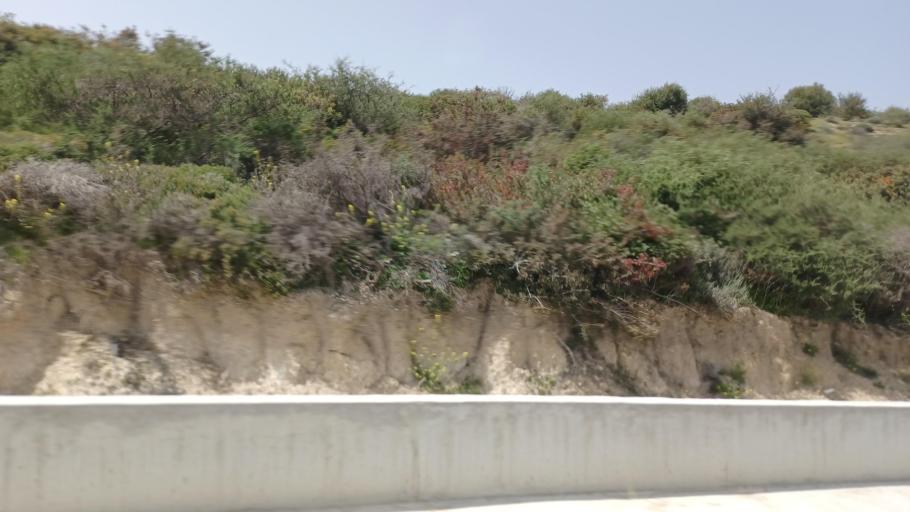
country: CY
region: Limassol
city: Pissouri
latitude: 34.7124
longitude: 32.7444
